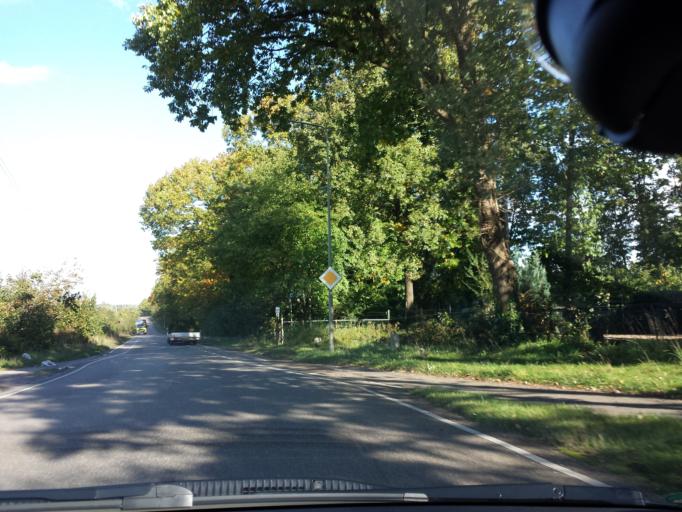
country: NL
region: Limburg
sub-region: Gemeente Brunssum
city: Brunssum
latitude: 50.9344
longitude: 6.0182
